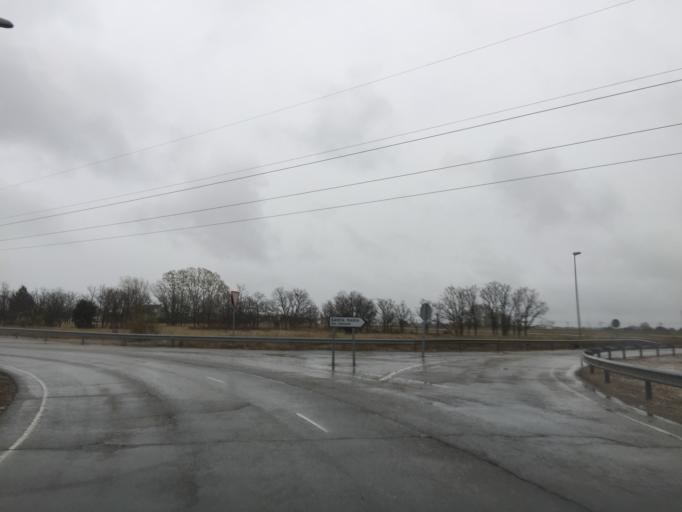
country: ES
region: Castille and Leon
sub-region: Provincia de Leon
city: Villadangos del Paramo
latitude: 42.5209
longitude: -5.7550
